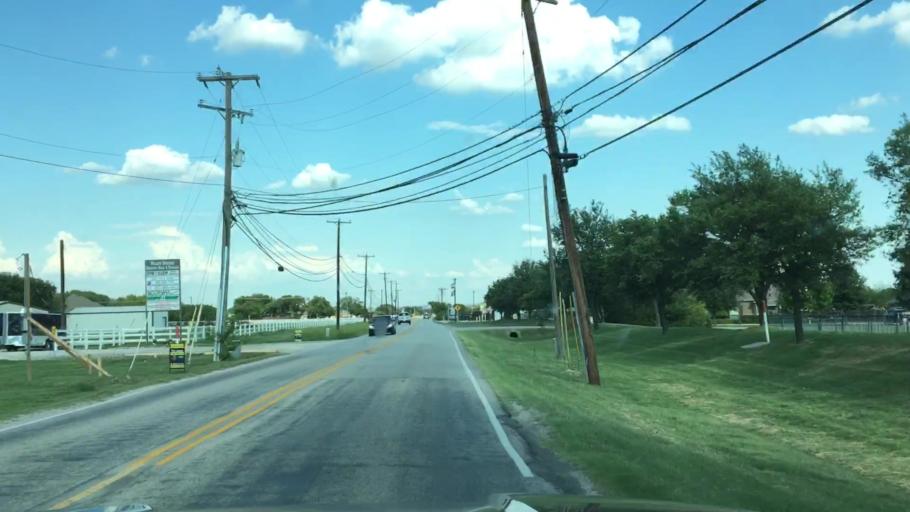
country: US
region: Texas
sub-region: Tarrant County
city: Haslet
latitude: 32.9688
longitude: -97.4014
